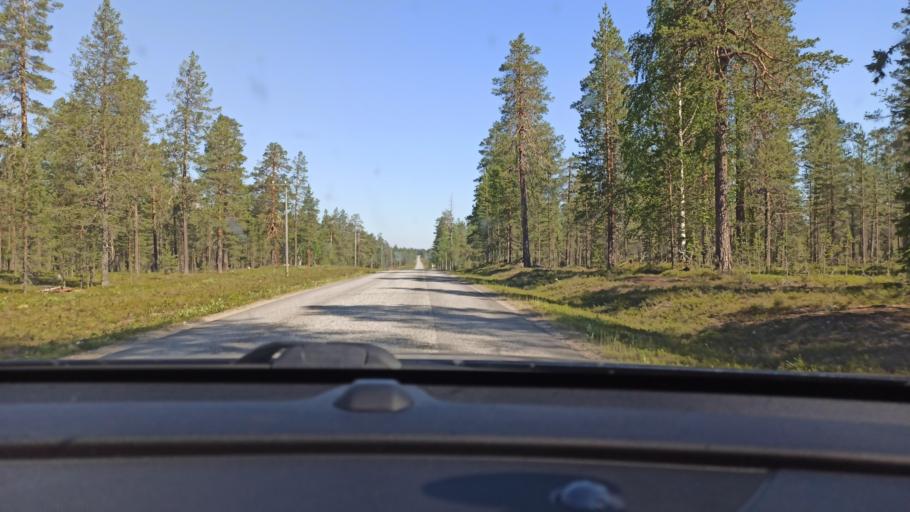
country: FI
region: Lapland
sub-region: Tunturi-Lappi
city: Kolari
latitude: 67.6421
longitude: 24.1584
